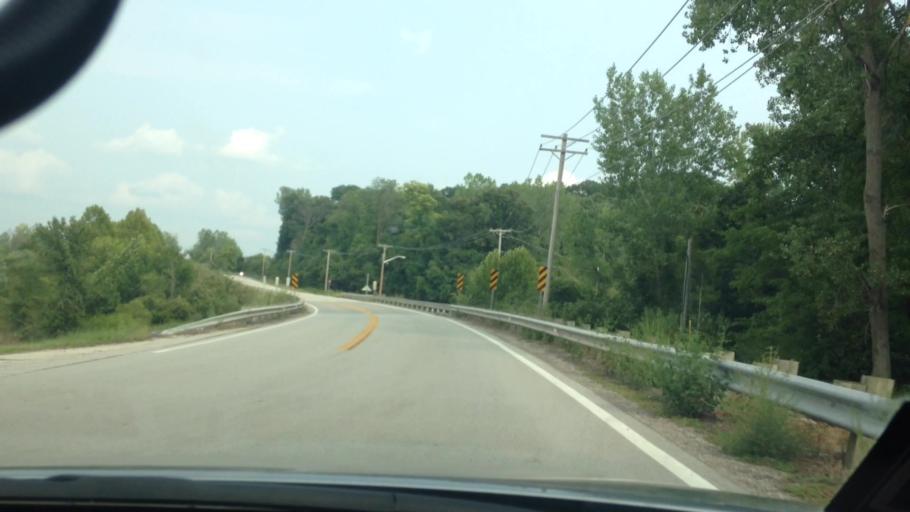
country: US
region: Kansas
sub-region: Leavenworth County
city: Lansing
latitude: 39.2013
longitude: -94.8222
